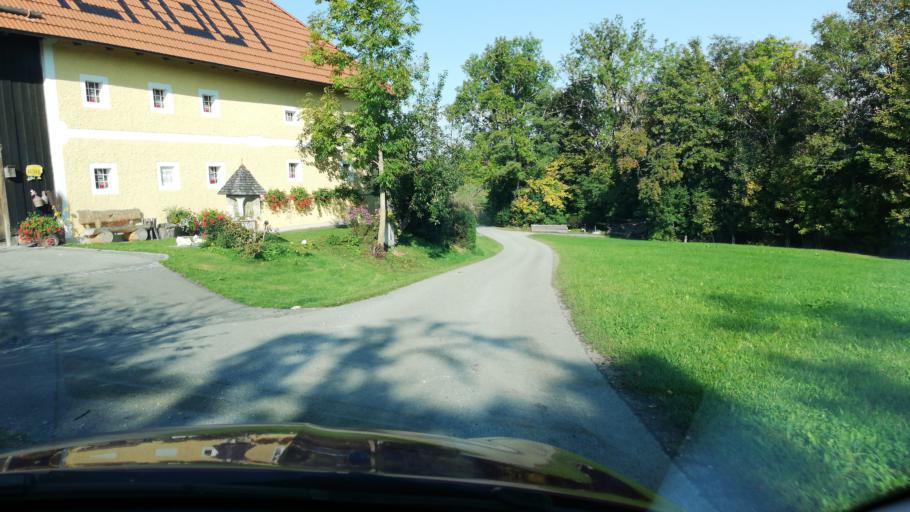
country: AT
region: Upper Austria
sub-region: Politischer Bezirk Kirchdorf an der Krems
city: Kremsmunster
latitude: 48.0957
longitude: 14.1635
